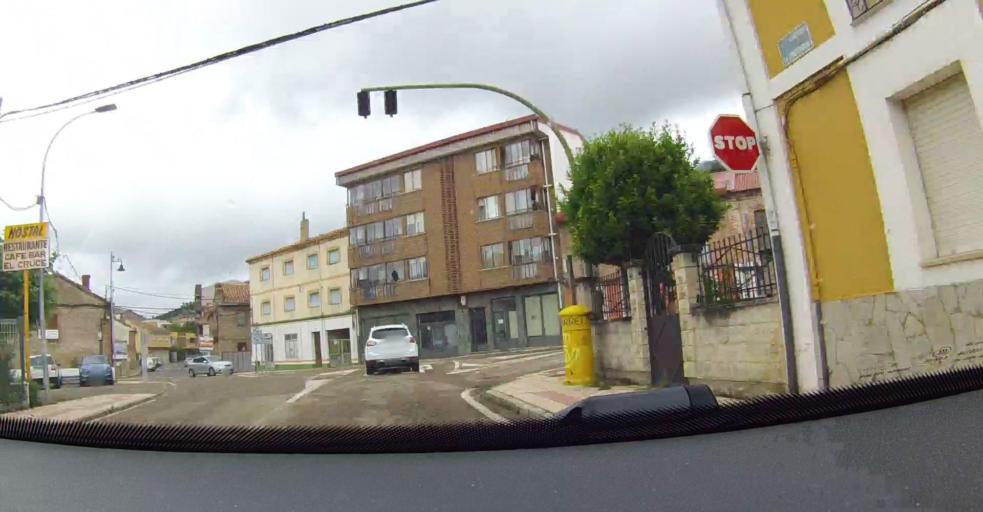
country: ES
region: Castille and Leon
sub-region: Provincia de Leon
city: Cistierna
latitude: 42.8003
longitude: -5.1254
